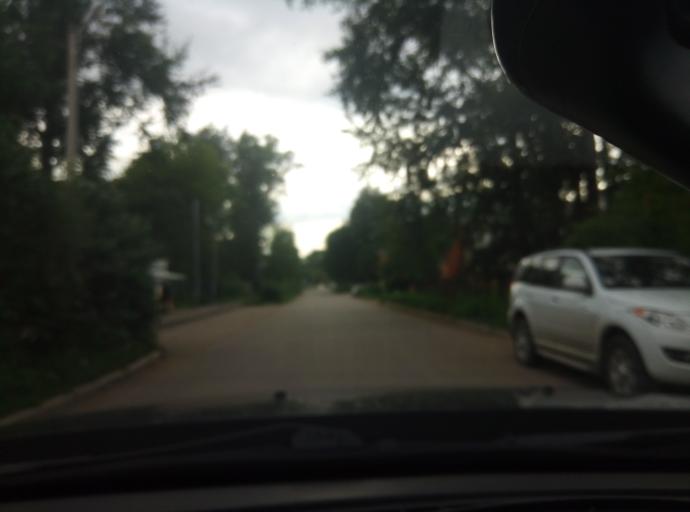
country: RU
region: Tula
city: Bolokhovo
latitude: 54.0841
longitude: 37.8277
